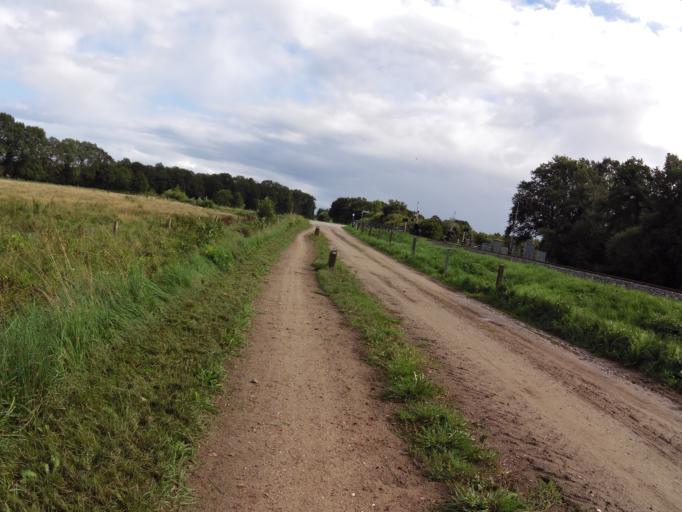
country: NL
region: Gelderland
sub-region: Gemeente Winterswijk
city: Winterswijk
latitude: 51.9867
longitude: 6.6707
